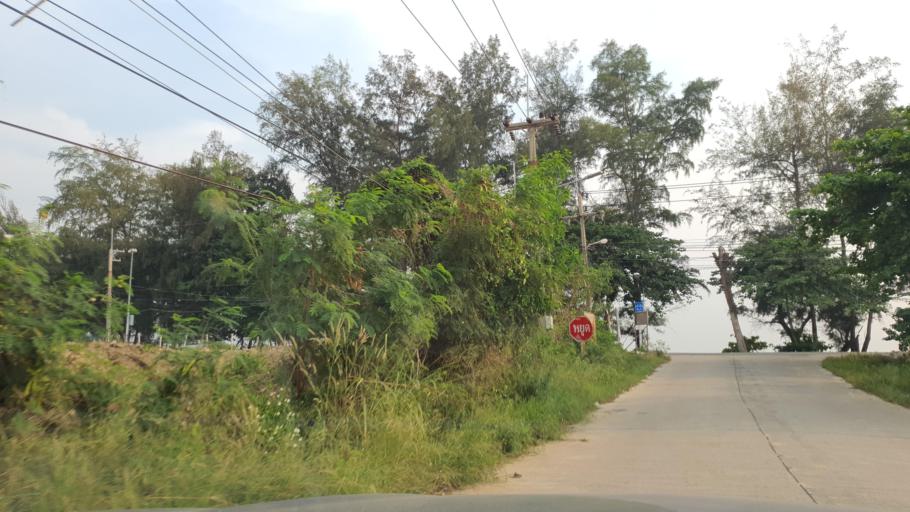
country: TH
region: Rayong
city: Rayong
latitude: 12.6039
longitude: 101.3991
